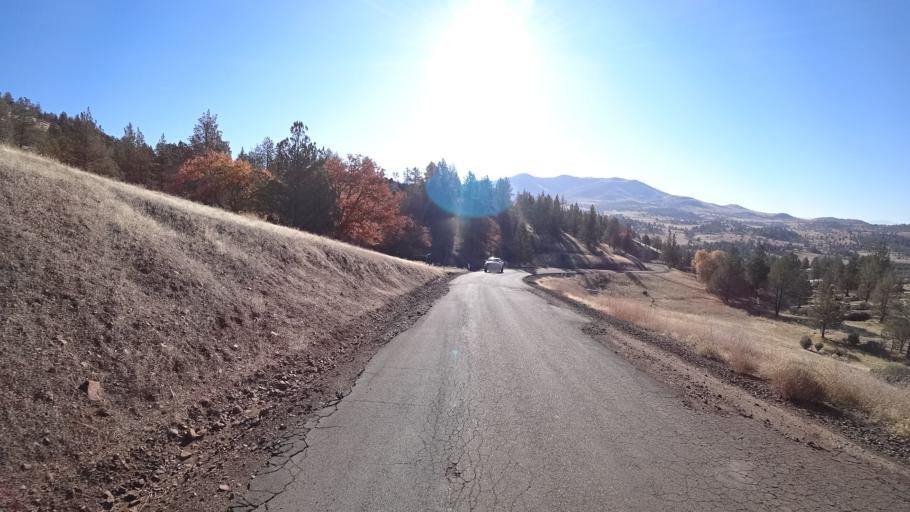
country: US
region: California
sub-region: Siskiyou County
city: Montague
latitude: 41.9009
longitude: -122.4249
